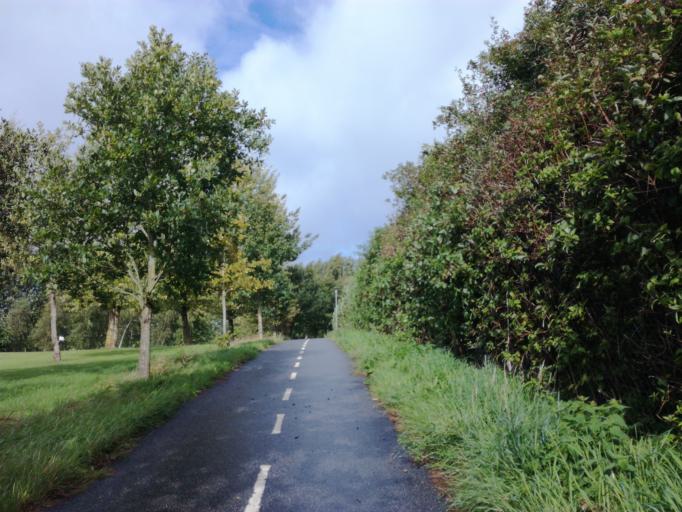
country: DK
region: South Denmark
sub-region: Fredericia Kommune
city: Fredericia
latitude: 55.5783
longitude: 9.7214
